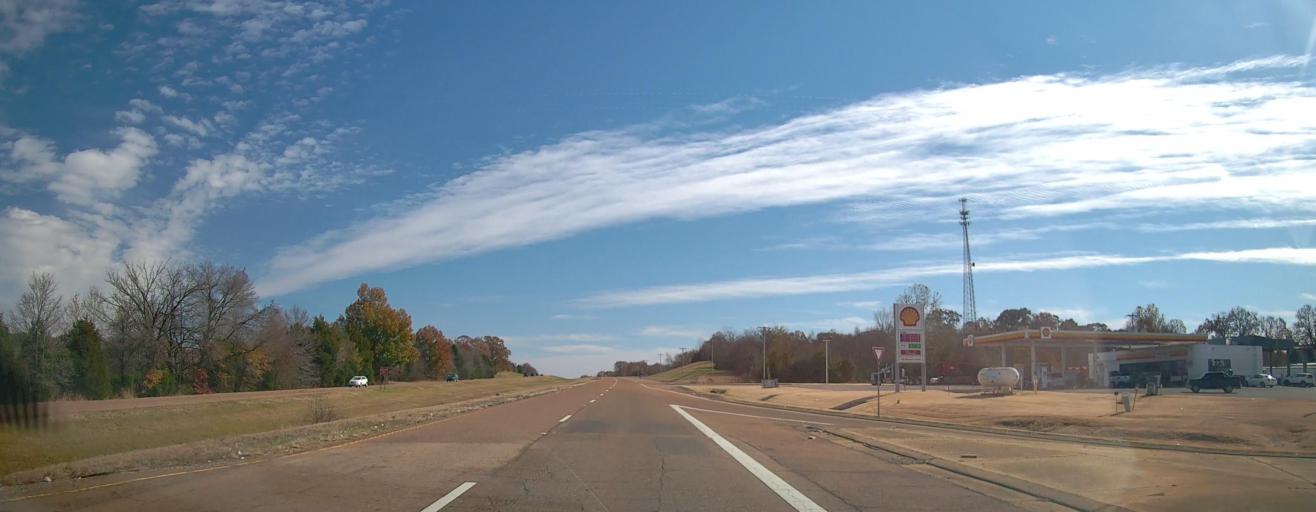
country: US
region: Tennessee
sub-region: Fayette County
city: Piperton
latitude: 34.9604
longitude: -89.5292
